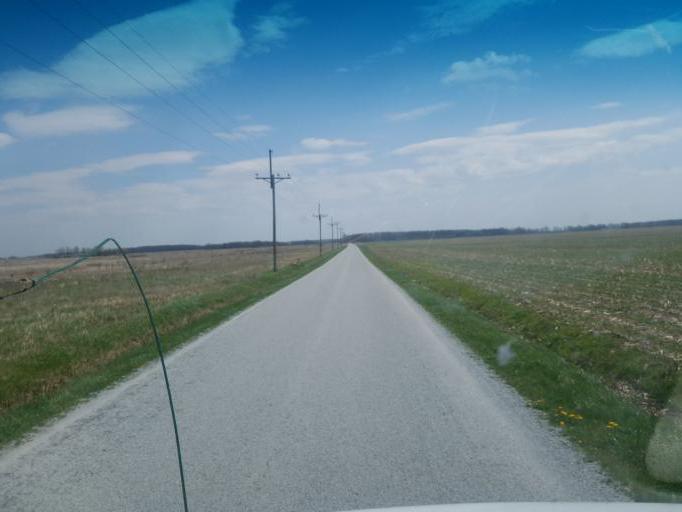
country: US
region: Ohio
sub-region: Hardin County
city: Forest
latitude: 40.7597
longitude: -83.5101
